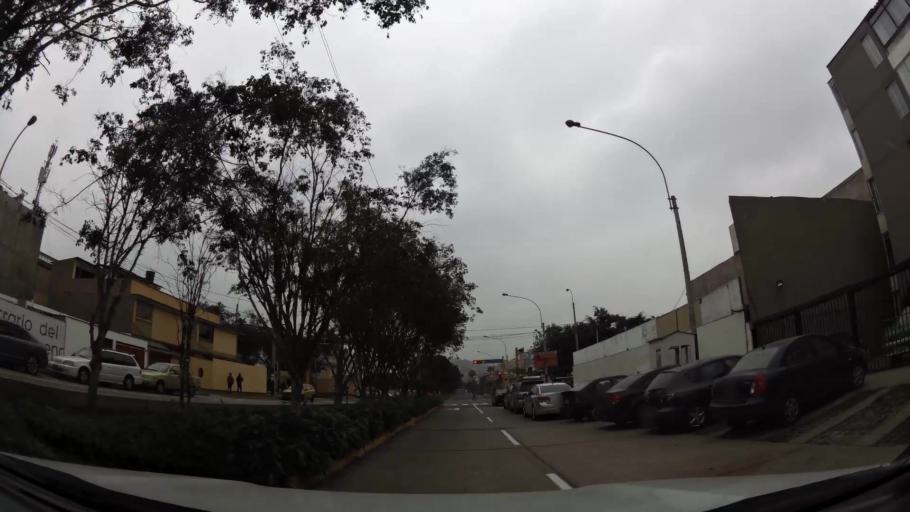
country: PE
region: Lima
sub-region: Lima
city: Surco
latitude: -12.1377
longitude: -76.9847
